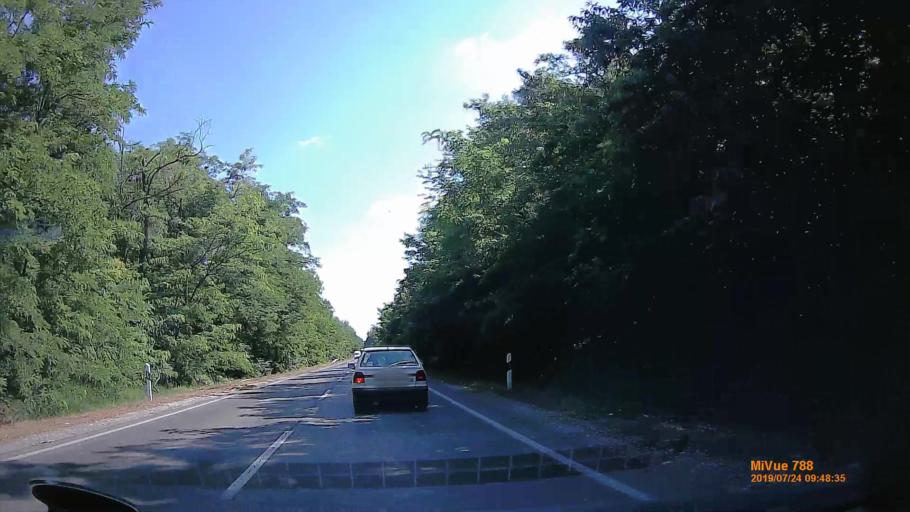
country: HU
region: Szabolcs-Szatmar-Bereg
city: Baktaloranthaza
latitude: 48.0046
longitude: 22.1180
